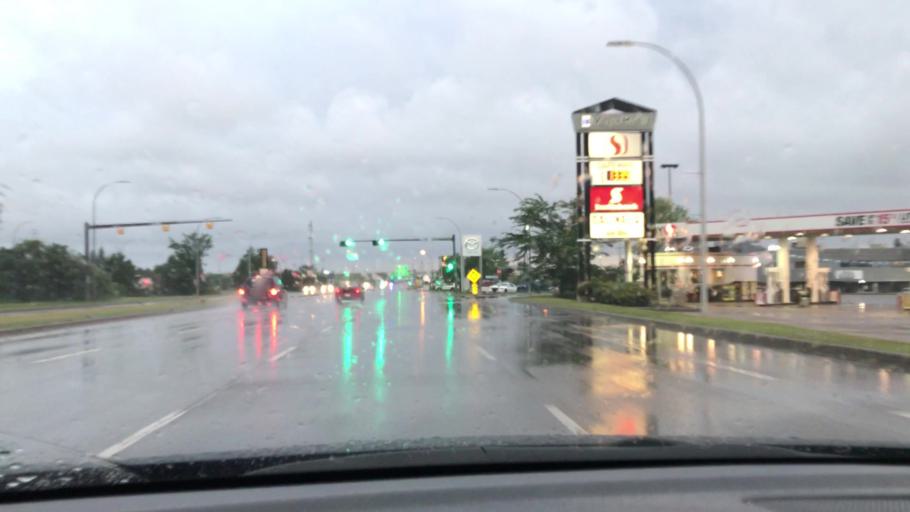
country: CA
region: Alberta
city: Sherwood Park
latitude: 53.5123
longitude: -113.3218
